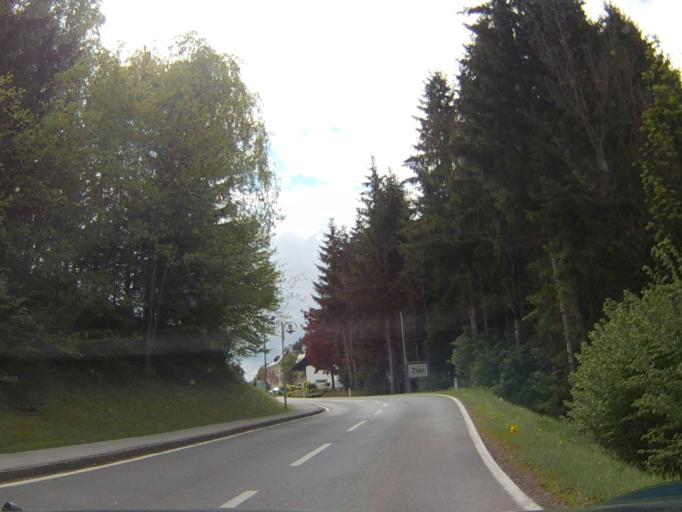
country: AT
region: Carinthia
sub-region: Politischer Bezirk Villach Land
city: Paternion
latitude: 46.7292
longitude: 13.5834
